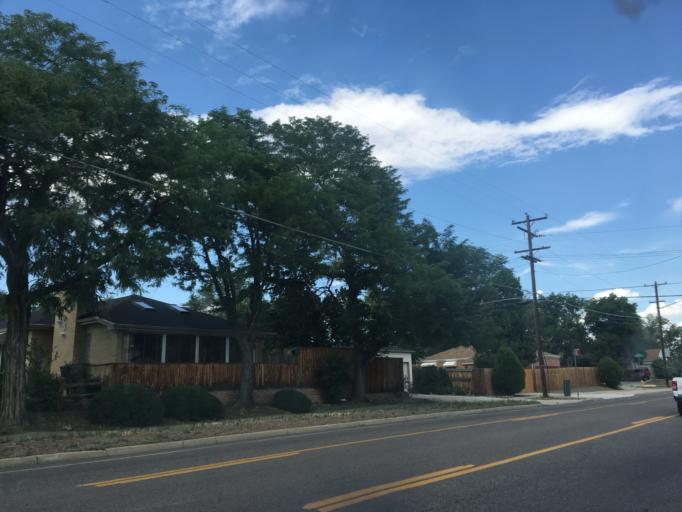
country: US
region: Colorado
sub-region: Jefferson County
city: Lakewood
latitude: 39.6894
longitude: -105.0510
